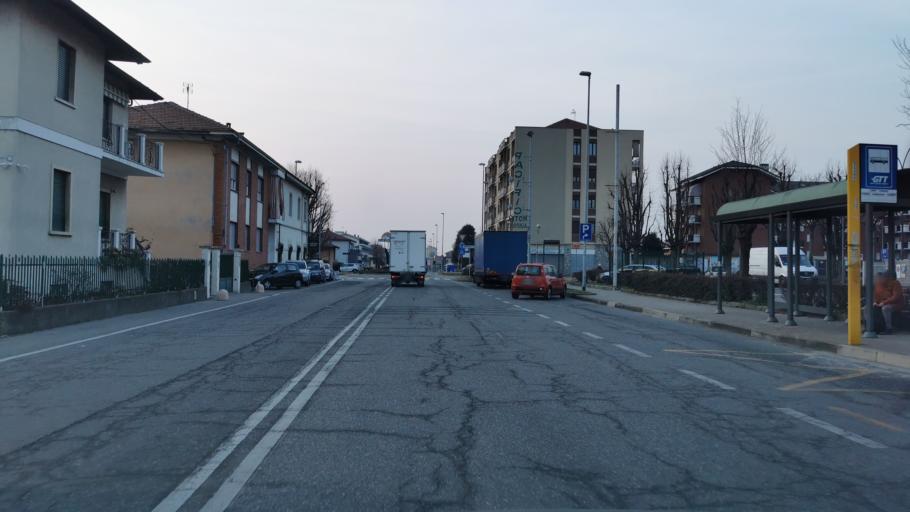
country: IT
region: Piedmont
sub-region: Provincia di Torino
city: Borgaro Torinese
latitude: 45.1527
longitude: 7.6547
